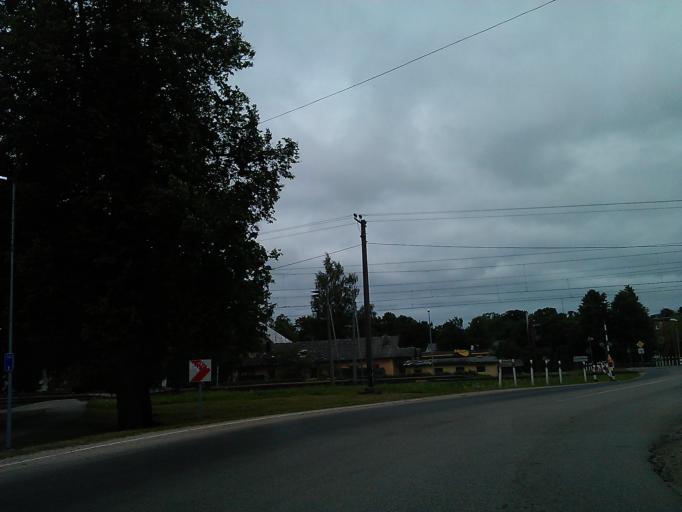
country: LV
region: Carnikava
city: Carnikava
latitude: 57.1288
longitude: 24.2809
